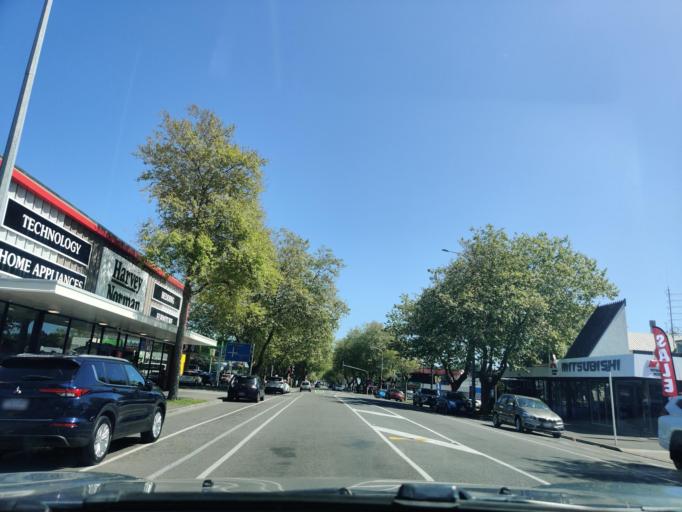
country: NZ
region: Manawatu-Wanganui
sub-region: Wanganui District
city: Wanganui
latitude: -39.9286
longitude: 175.0447
